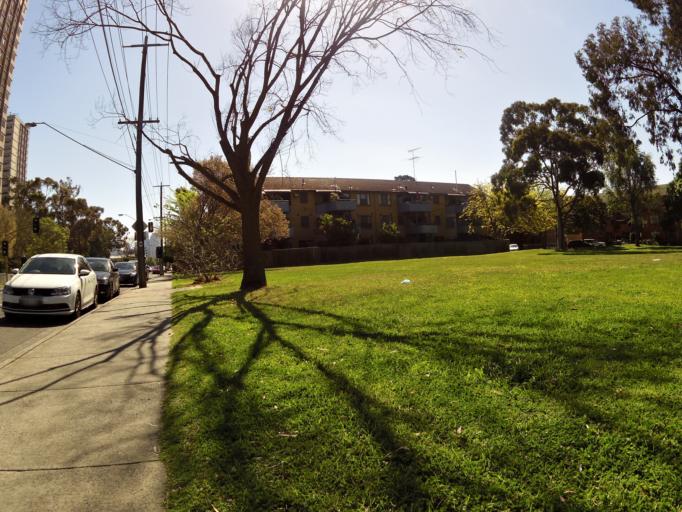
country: AU
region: Victoria
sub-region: Yarra
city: Richmond
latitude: -37.8117
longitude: 144.9983
